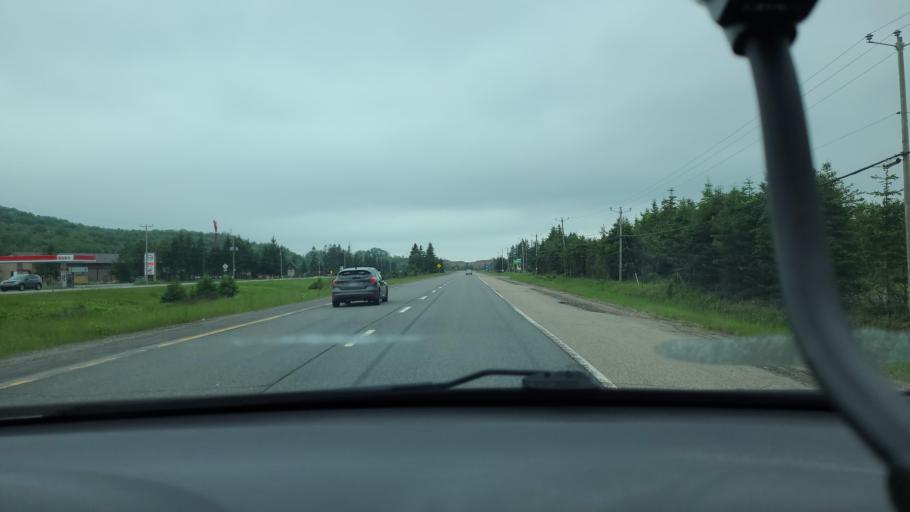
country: CA
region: Quebec
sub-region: Laurentides
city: Mont-Tremblant
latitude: 46.1231
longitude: -74.4518
